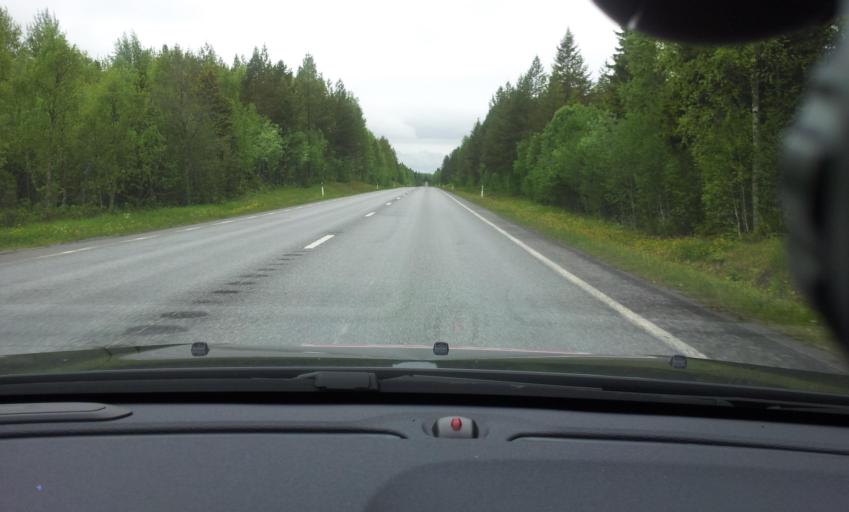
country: SE
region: Jaemtland
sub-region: Krokoms Kommun
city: Krokom
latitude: 63.3214
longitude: 14.2478
